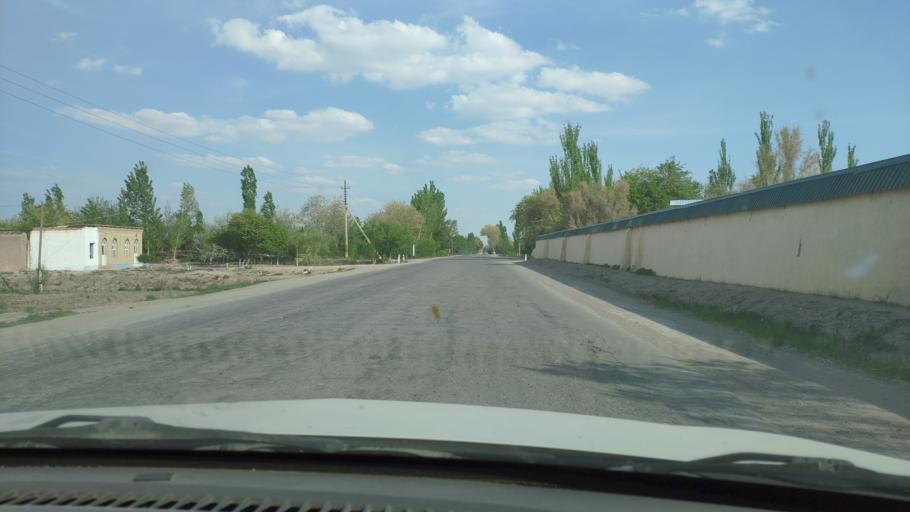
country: UZ
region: Karakalpakstan
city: Beruniy
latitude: 41.6041
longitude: 60.8606
